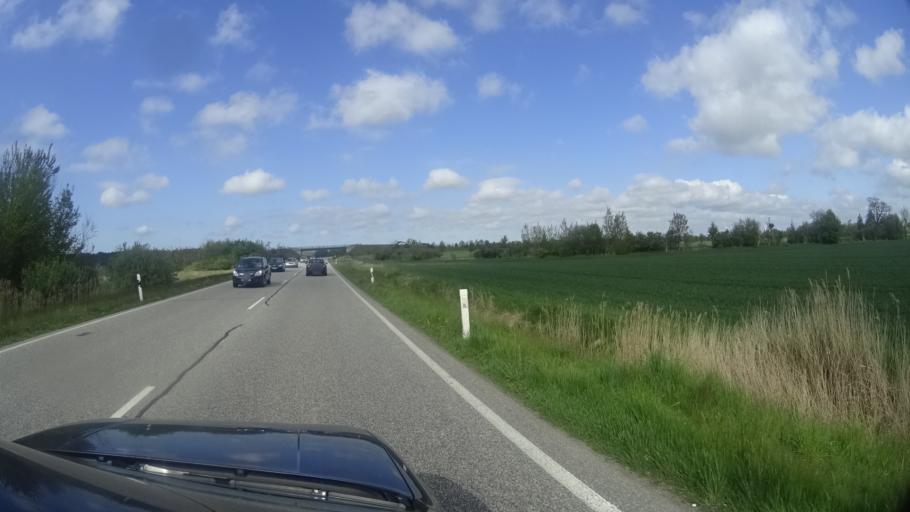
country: DE
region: Mecklenburg-Vorpommern
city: Bentwisch
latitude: 54.1239
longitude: 12.2034
